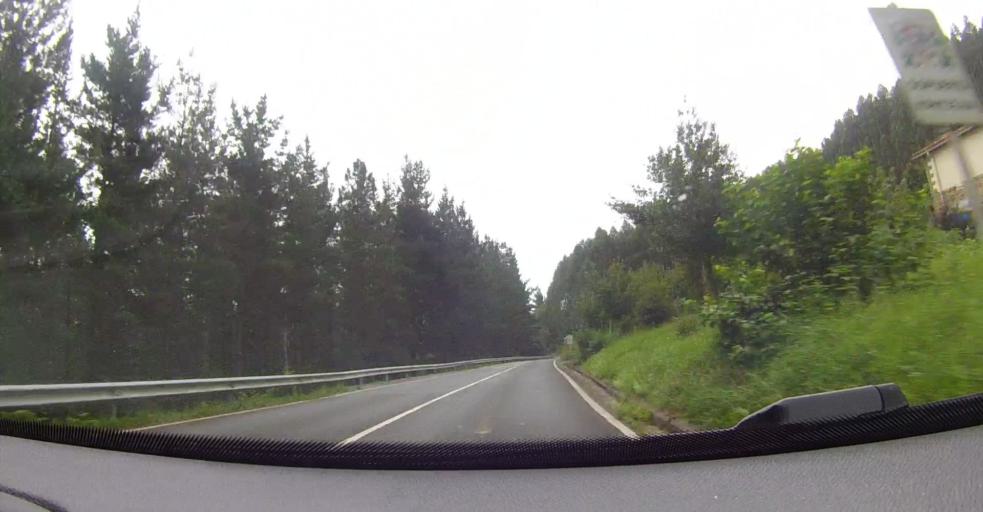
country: ES
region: Basque Country
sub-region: Bizkaia
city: Balmaseda
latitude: 43.2304
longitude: -3.1972
